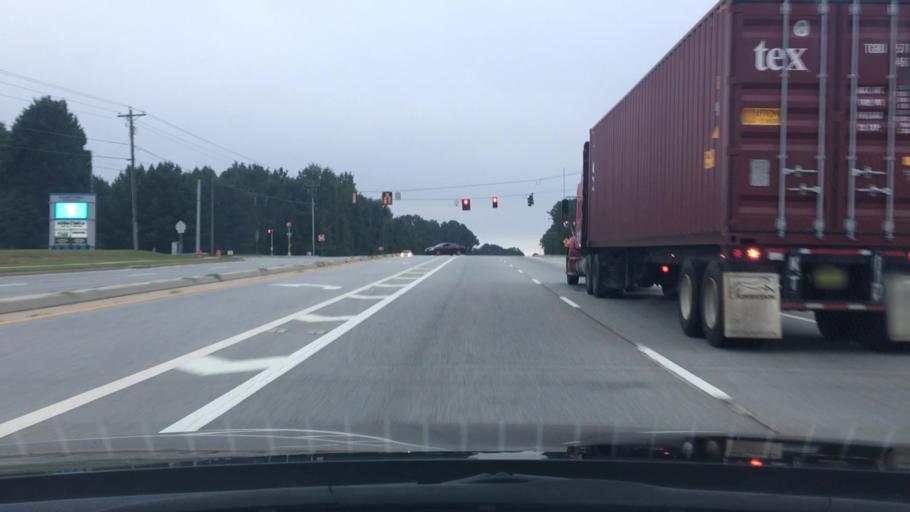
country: US
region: Georgia
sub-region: Coweta County
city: Senoia
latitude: 33.3407
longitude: -84.5229
